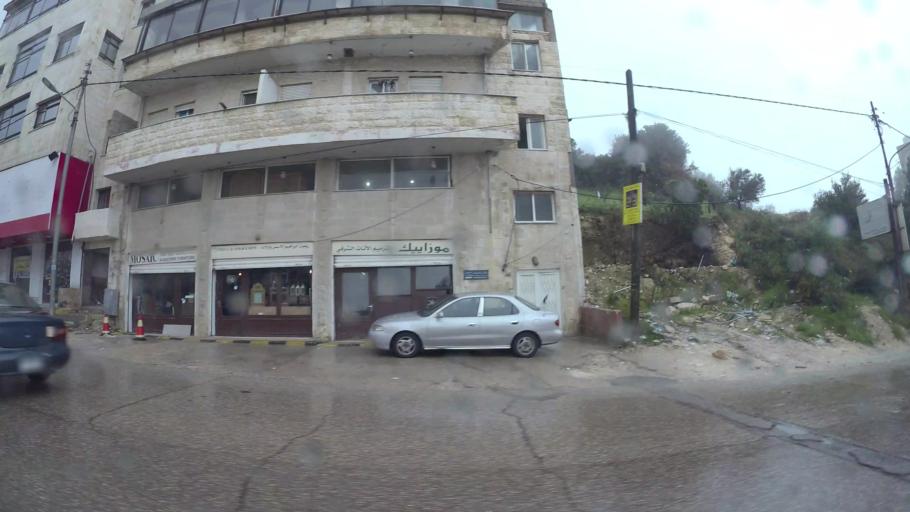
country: JO
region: Amman
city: Wadi as Sir
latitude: 32.0022
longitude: 35.7892
